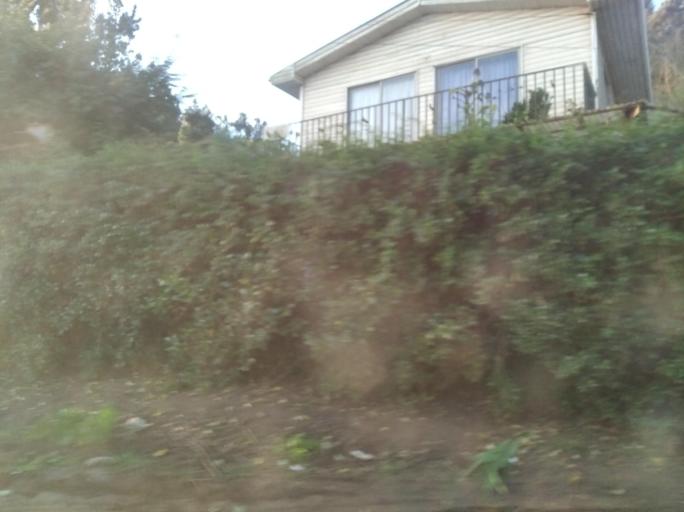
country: CL
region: Valparaiso
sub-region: San Antonio Province
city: El Tabo
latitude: -33.4531
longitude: -71.6518
